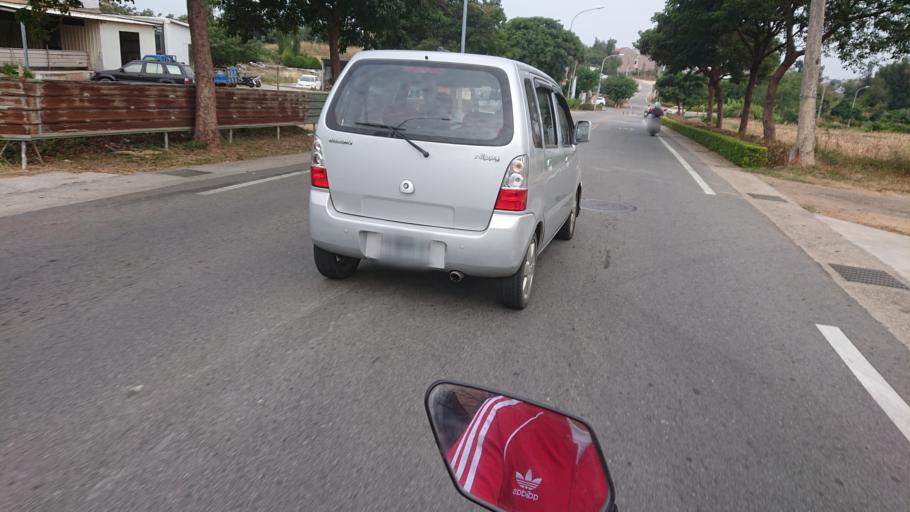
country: TW
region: Fukien
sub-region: Kinmen
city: Jincheng
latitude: 24.4202
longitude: 118.3108
